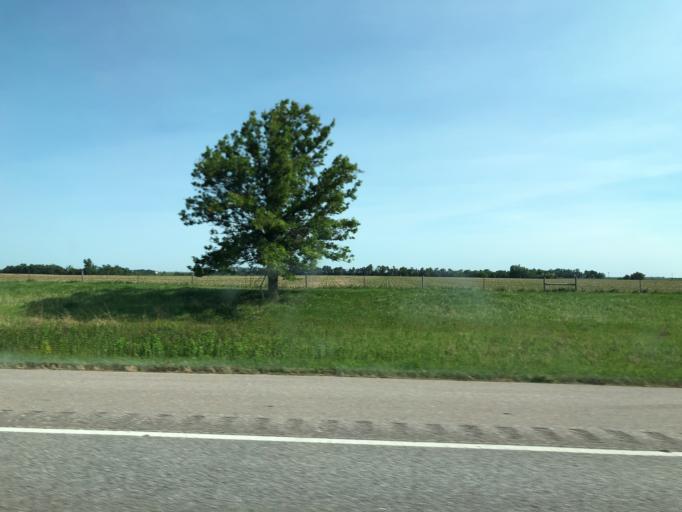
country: US
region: Nebraska
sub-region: Seward County
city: Seward
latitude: 40.8222
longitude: -97.1569
